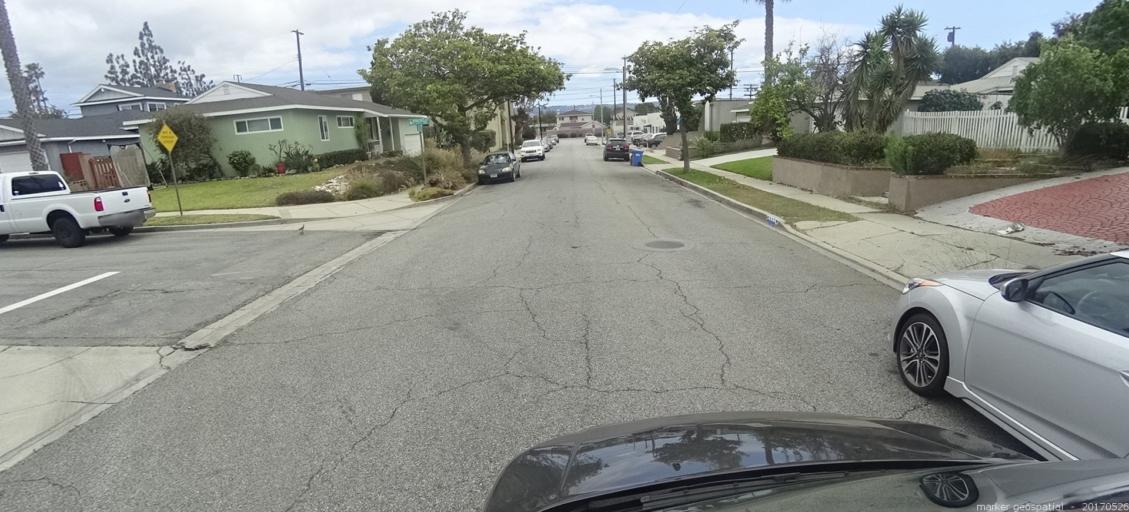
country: US
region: California
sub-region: Los Angeles County
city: Lawndale
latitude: 33.8597
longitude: -118.3557
